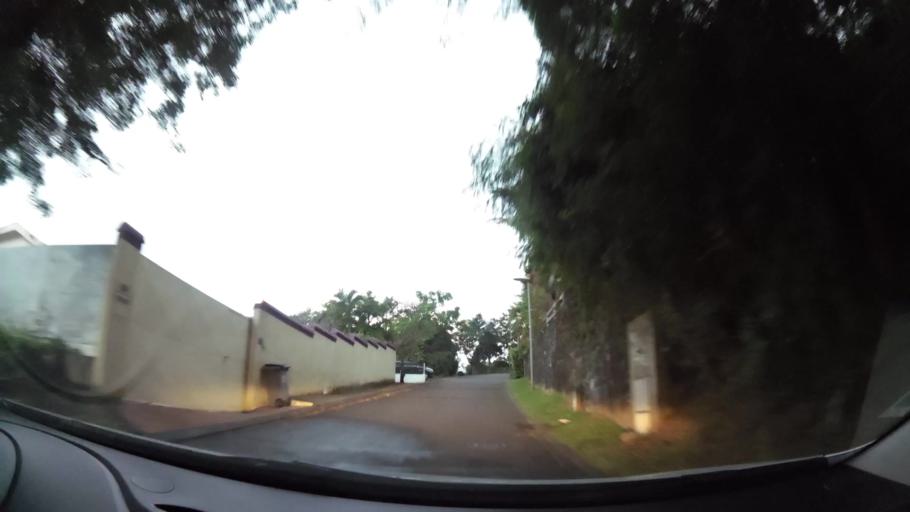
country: RE
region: Reunion
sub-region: Reunion
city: Saint-Denis
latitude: -20.9087
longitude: 55.4664
